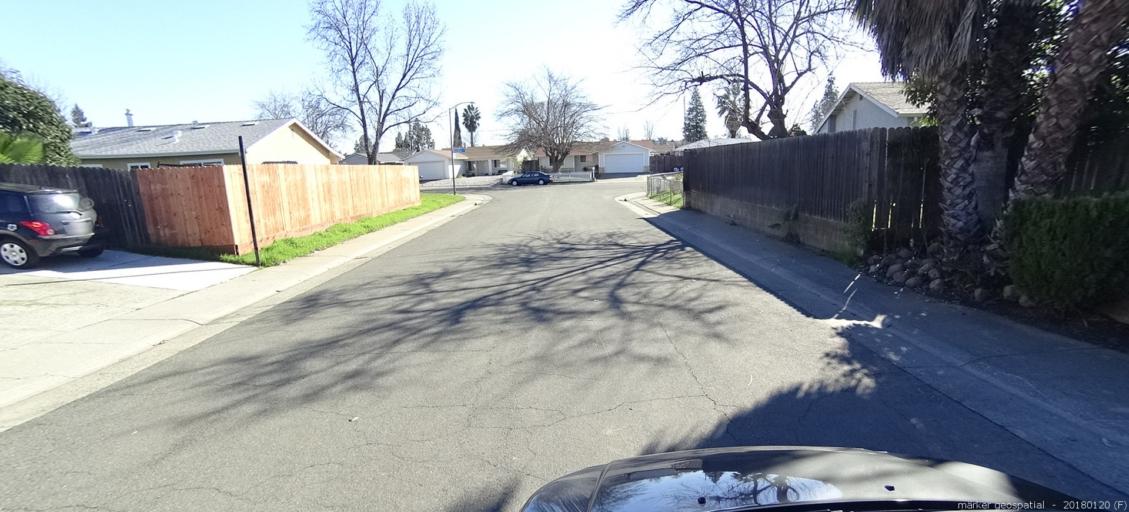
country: US
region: California
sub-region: Sacramento County
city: La Riviera
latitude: 38.5603
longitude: -121.3228
